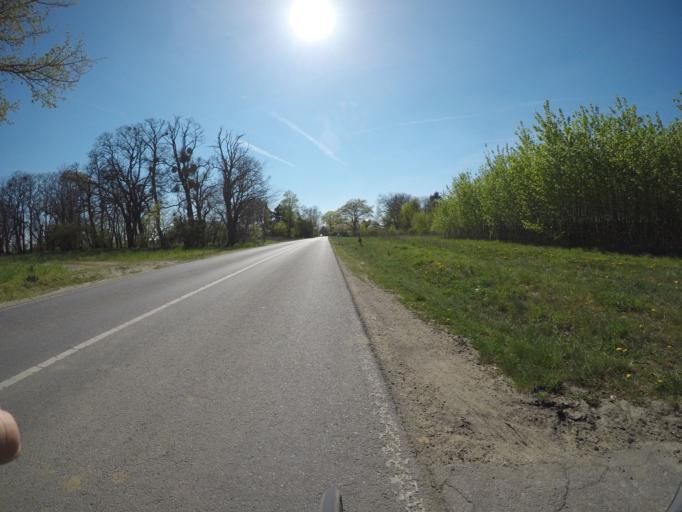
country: DE
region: Brandenburg
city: Rehfelde
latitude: 52.5566
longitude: 13.9521
